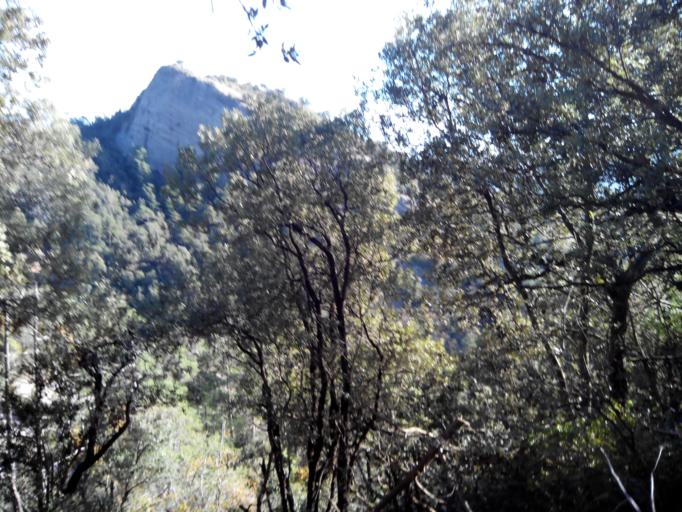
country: ES
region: Catalonia
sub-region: Provincia de Barcelona
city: Vilada
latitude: 42.1130
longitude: 1.9368
